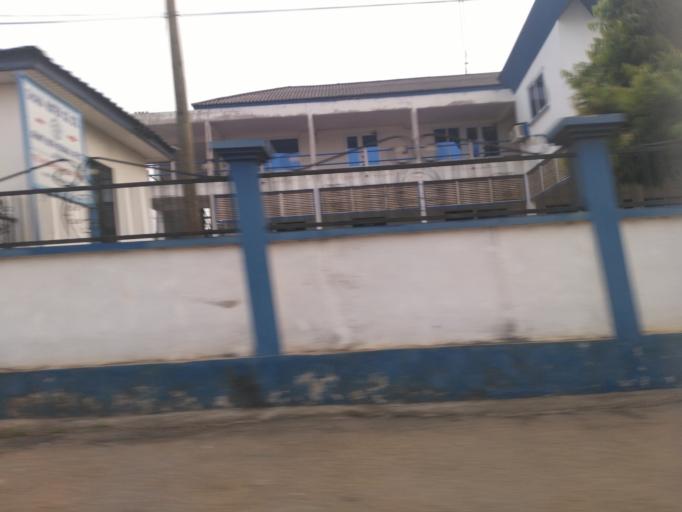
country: GH
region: Ashanti
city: Kumasi
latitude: 6.6835
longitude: -1.6196
